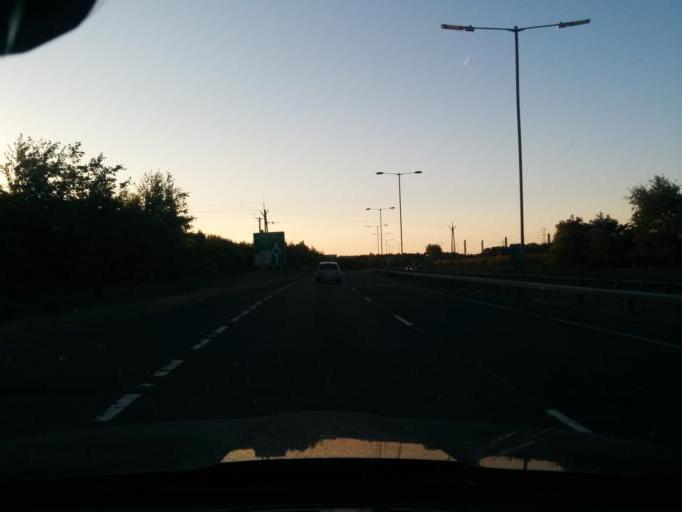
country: GB
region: England
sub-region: Northumberland
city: Newbiggin-by-the-Sea
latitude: 55.1846
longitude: -1.5380
